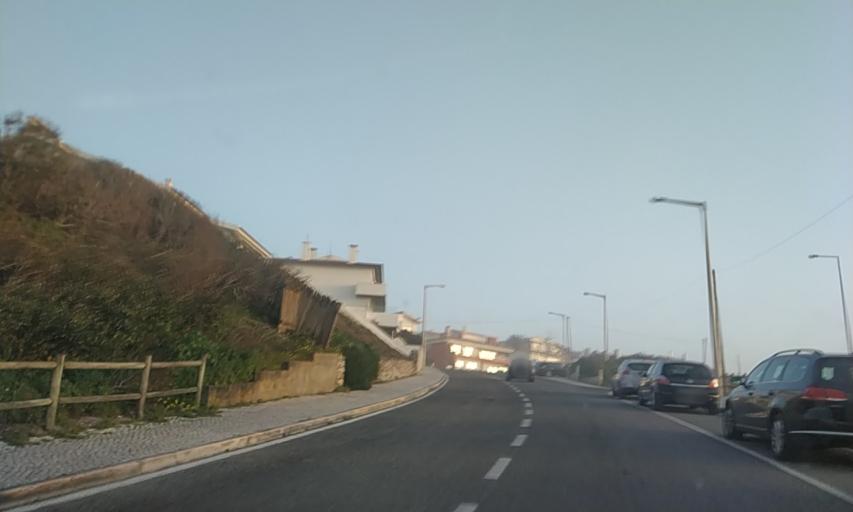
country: PT
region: Leiria
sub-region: Alcobaca
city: Pataias
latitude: 39.7548
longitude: -9.0322
